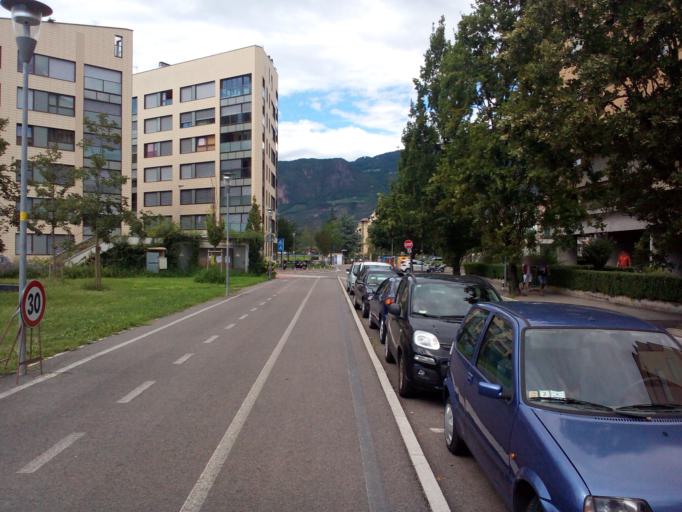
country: IT
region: Trentino-Alto Adige
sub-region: Bolzano
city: Bolzano
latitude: 46.4819
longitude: 11.3170
